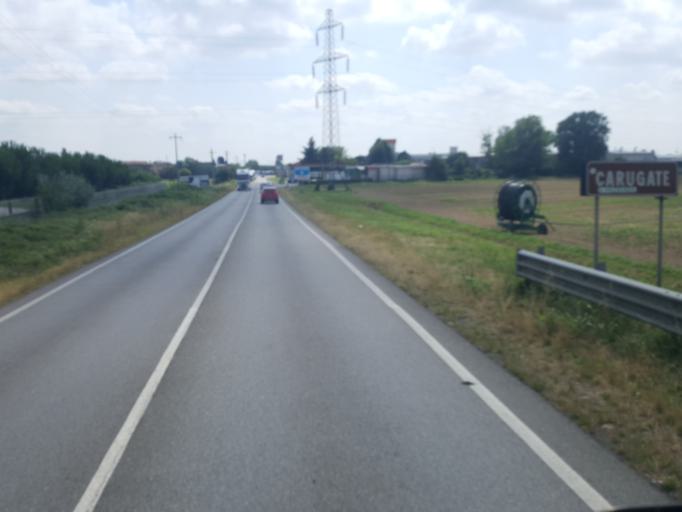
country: IT
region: Lombardy
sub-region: Citta metropolitana di Milano
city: Carugate
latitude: 45.5614
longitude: 9.3388
